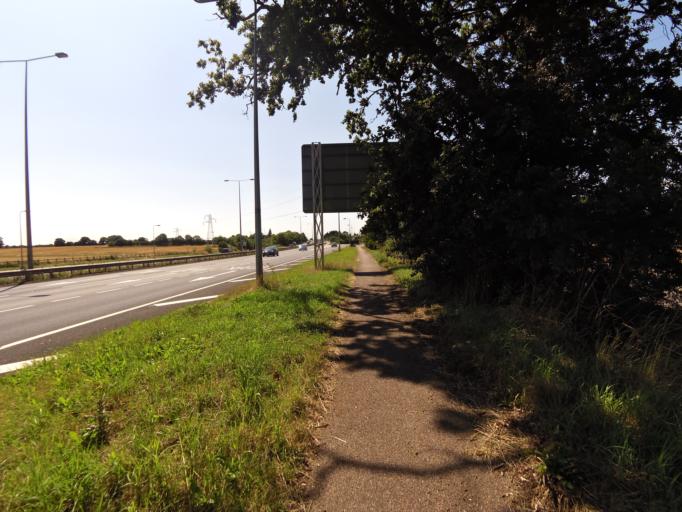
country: GB
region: England
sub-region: Suffolk
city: Capel Saint Mary
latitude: 52.0076
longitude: 1.0609
